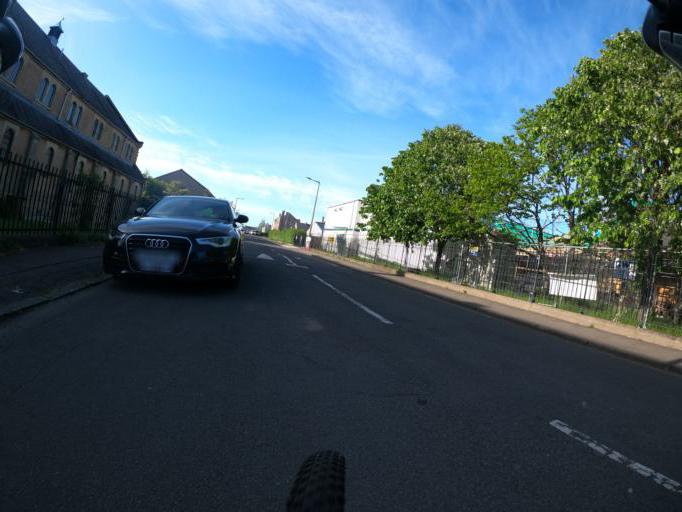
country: GB
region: Scotland
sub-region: Edinburgh
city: Edinburgh
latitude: 55.9758
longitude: -3.2276
